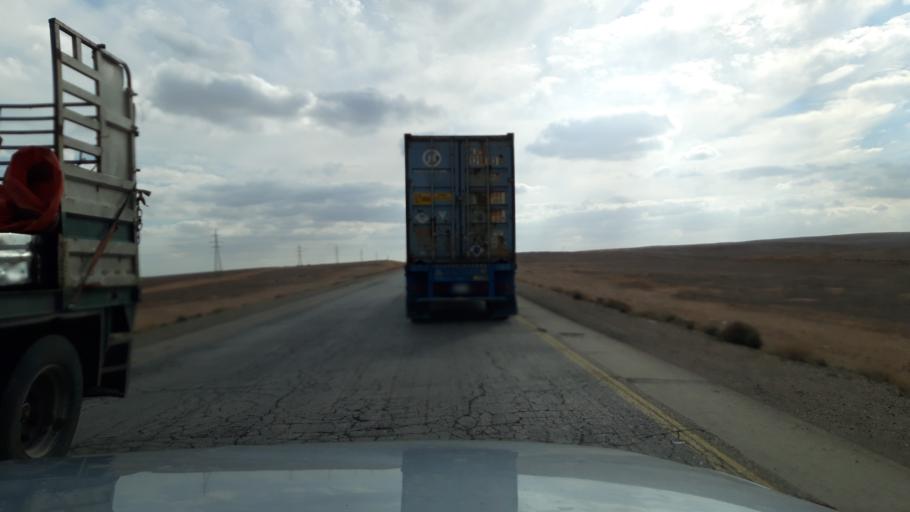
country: JO
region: Amman
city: Al Azraq ash Shamali
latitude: 31.7570
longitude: 36.5489
